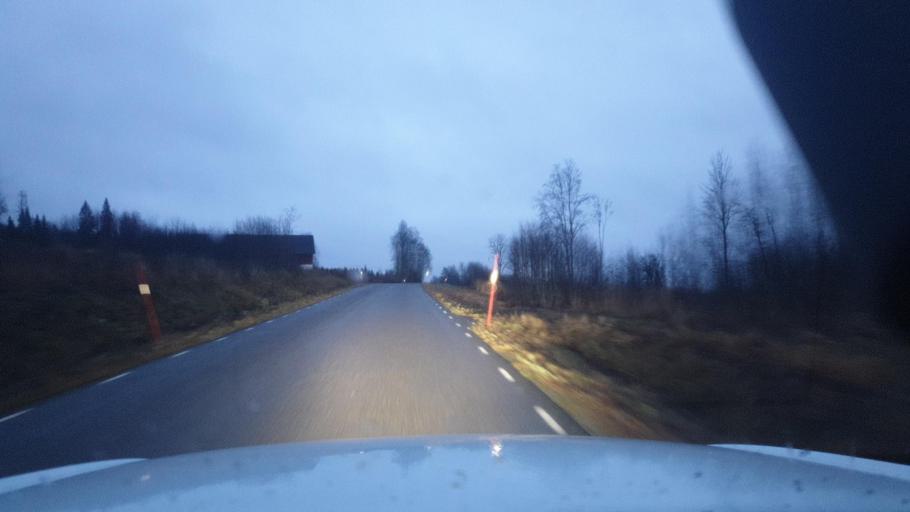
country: SE
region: Vaermland
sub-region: Torsby Kommun
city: Torsby
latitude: 60.0126
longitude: 12.6683
